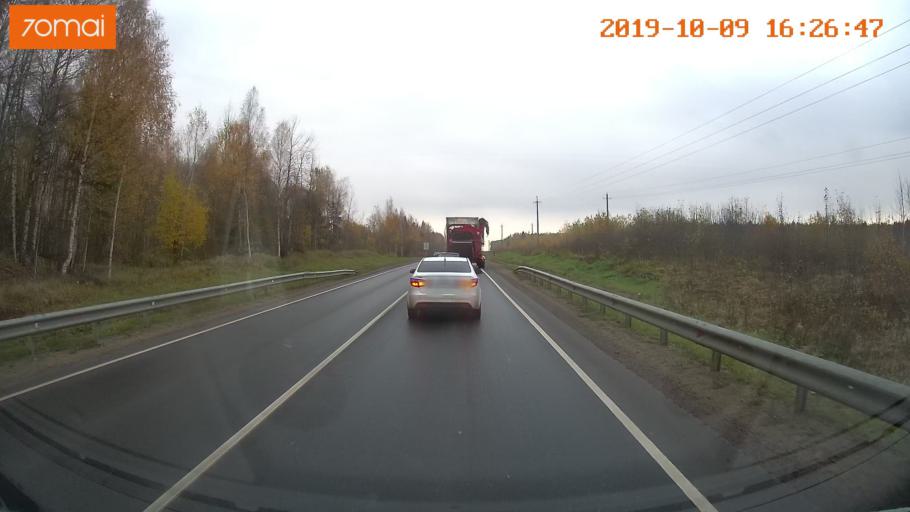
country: RU
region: Kostroma
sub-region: Kostromskoy Rayon
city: Kostroma
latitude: 57.6361
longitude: 40.9255
